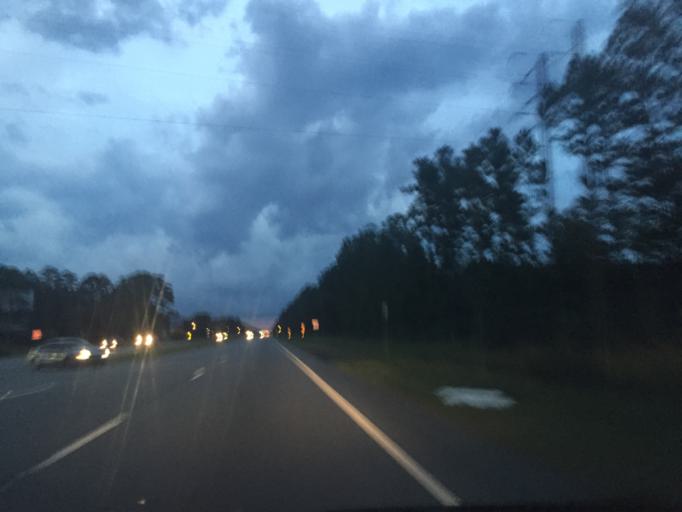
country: US
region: Georgia
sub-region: Bryan County
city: Richmond Hill
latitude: 31.8965
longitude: -81.3737
